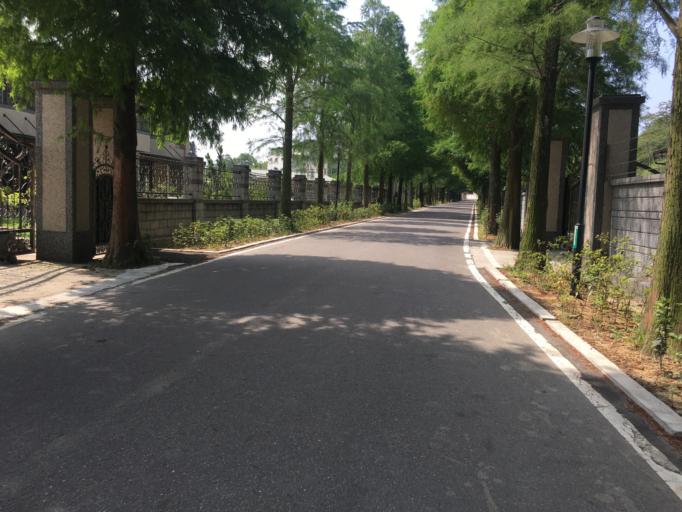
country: TW
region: Taiwan
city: Daxi
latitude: 24.8715
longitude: 121.2558
